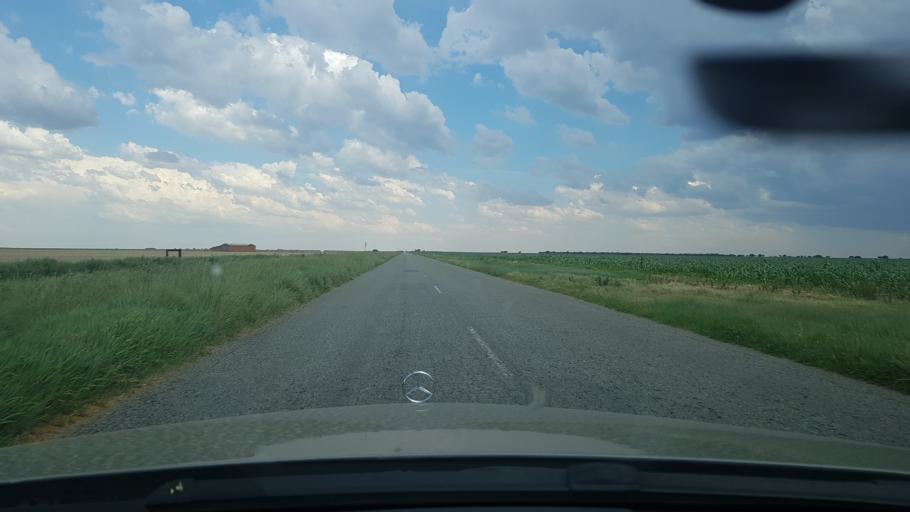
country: ZA
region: Orange Free State
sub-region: Lejweleputswa District Municipality
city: Hoopstad
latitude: -27.8899
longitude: 25.6689
